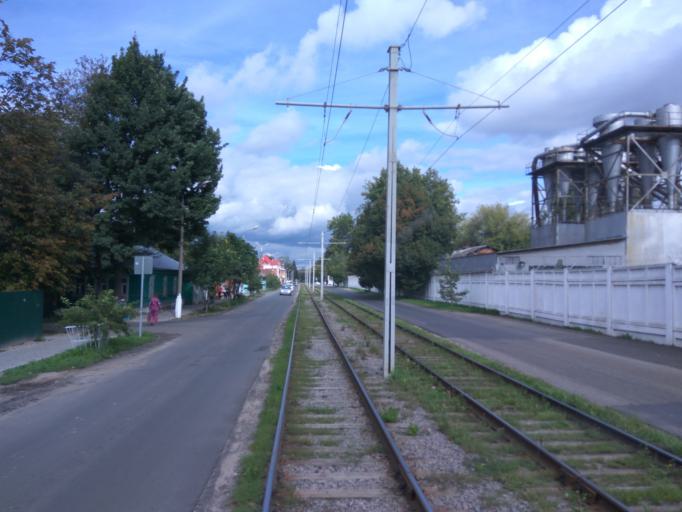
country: RU
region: Moskovskaya
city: Kolomna
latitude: 55.0969
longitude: 38.7726
